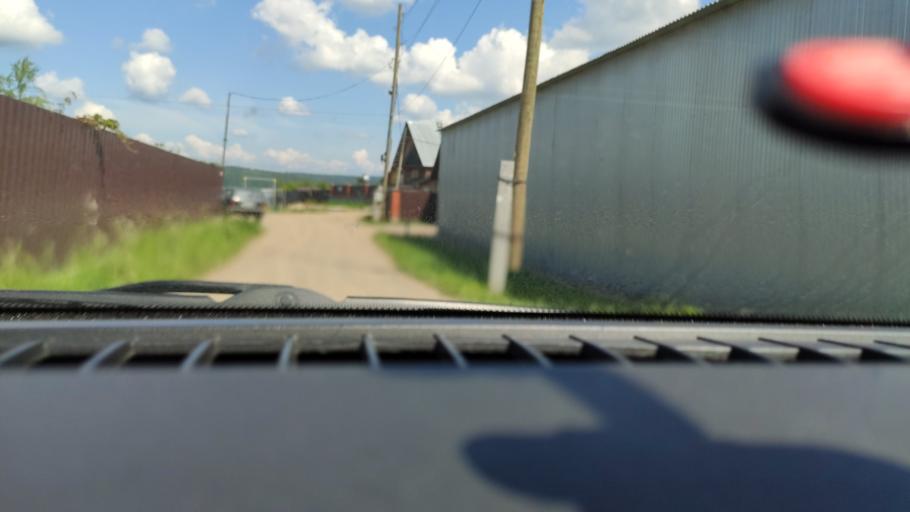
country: RU
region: Perm
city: Sylva
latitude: 58.0475
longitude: 56.7261
